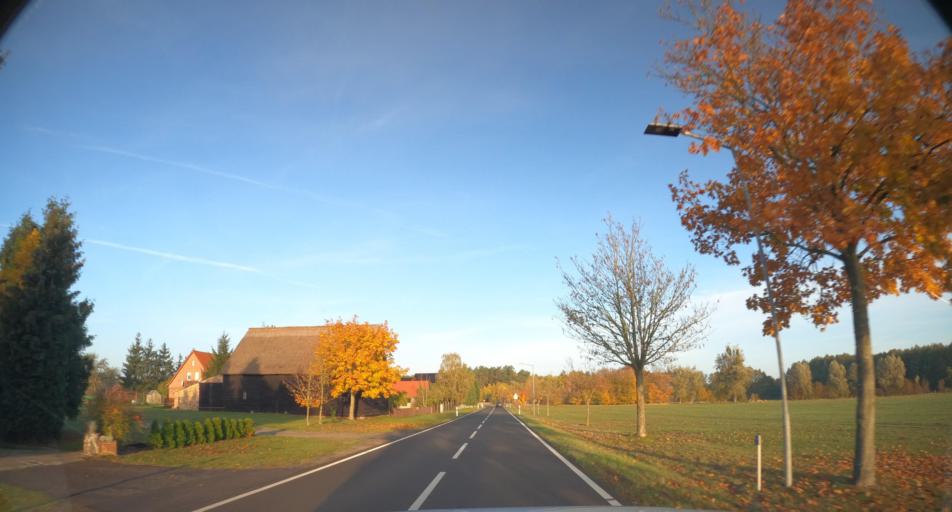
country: DE
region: Mecklenburg-Vorpommern
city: Ahlbeck
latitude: 53.6463
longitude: 14.1960
